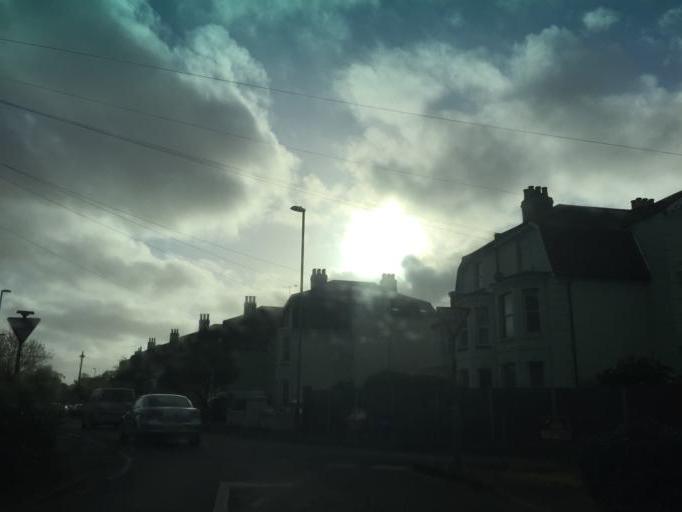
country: GB
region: England
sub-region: Hampshire
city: Gosport
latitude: 50.7916
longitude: -1.1397
